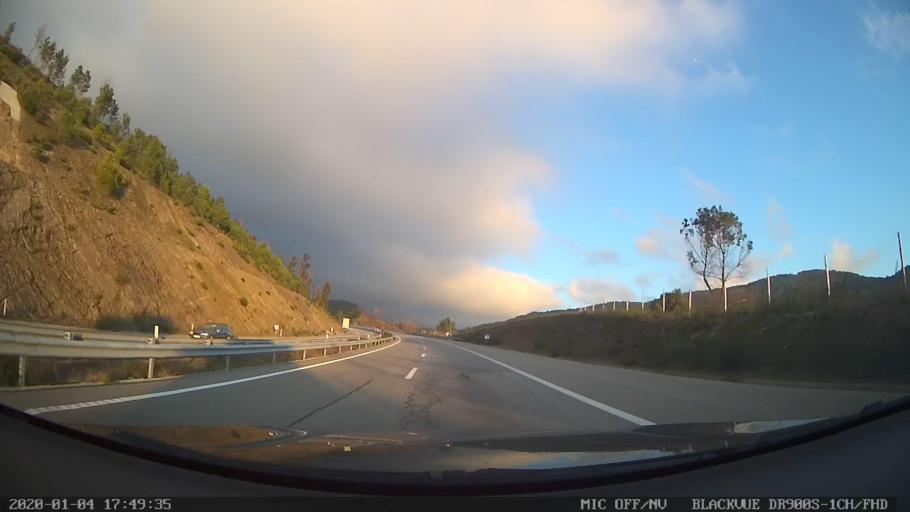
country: PT
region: Vila Real
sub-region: Ribeira de Pena
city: Ribeira de Pena
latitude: 41.4910
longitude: -7.8457
